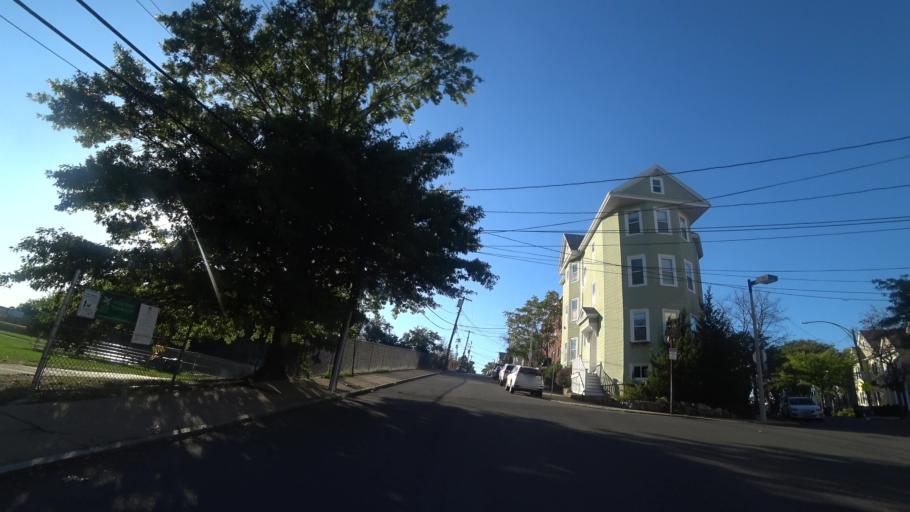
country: US
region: Massachusetts
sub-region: Norfolk County
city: Brookline
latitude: 42.3282
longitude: -71.1002
